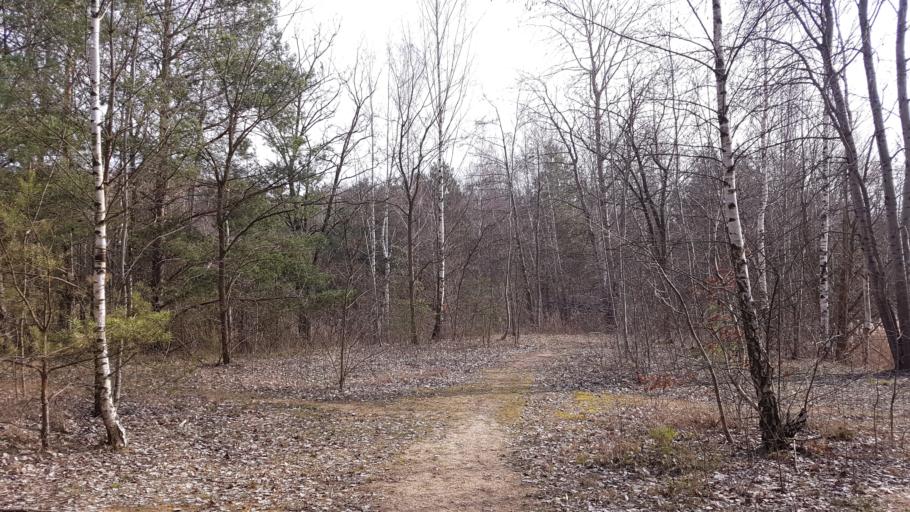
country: DE
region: Brandenburg
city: Doberlug-Kirchhain
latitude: 51.6267
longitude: 13.5719
